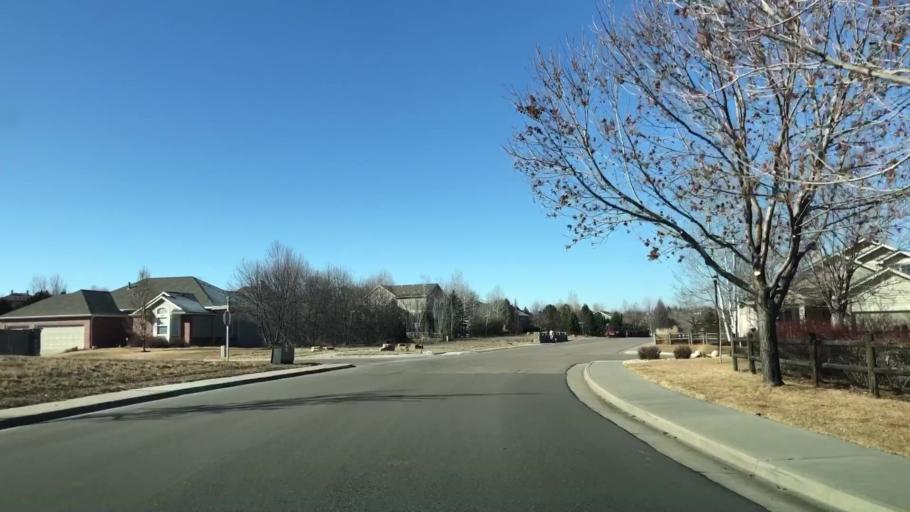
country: US
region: Colorado
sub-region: Weld County
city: Windsor
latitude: 40.4721
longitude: -104.9477
